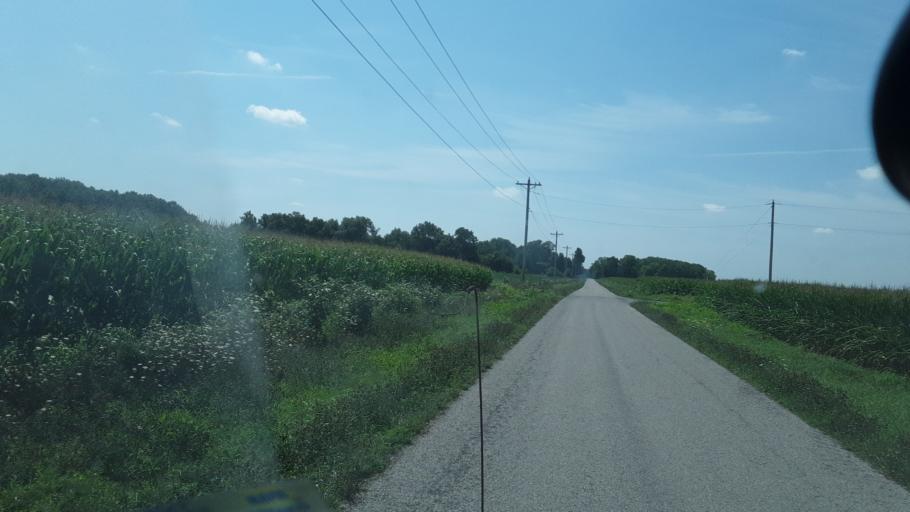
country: US
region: Ohio
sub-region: Hancock County
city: Findlay
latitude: 40.9720
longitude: -83.5553
